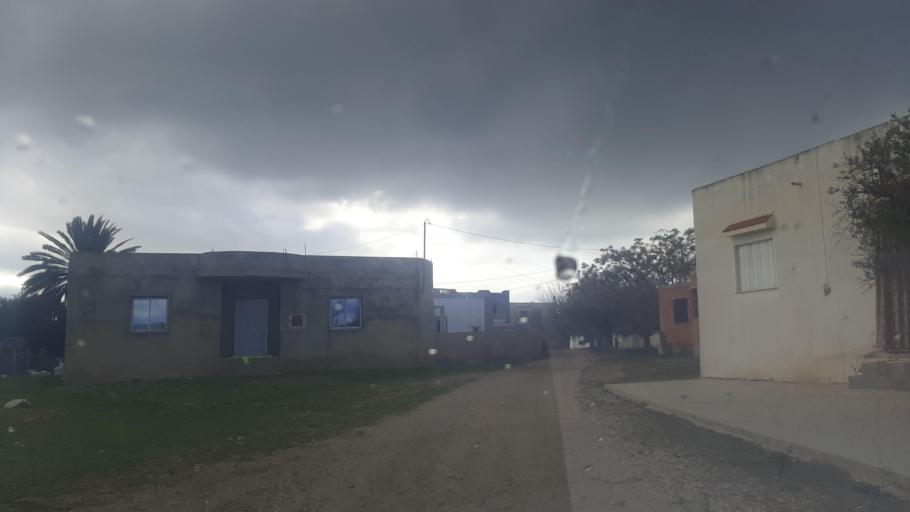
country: TN
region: Nabul
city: Manzil Bu Zalafah
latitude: 36.7352
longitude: 10.5243
